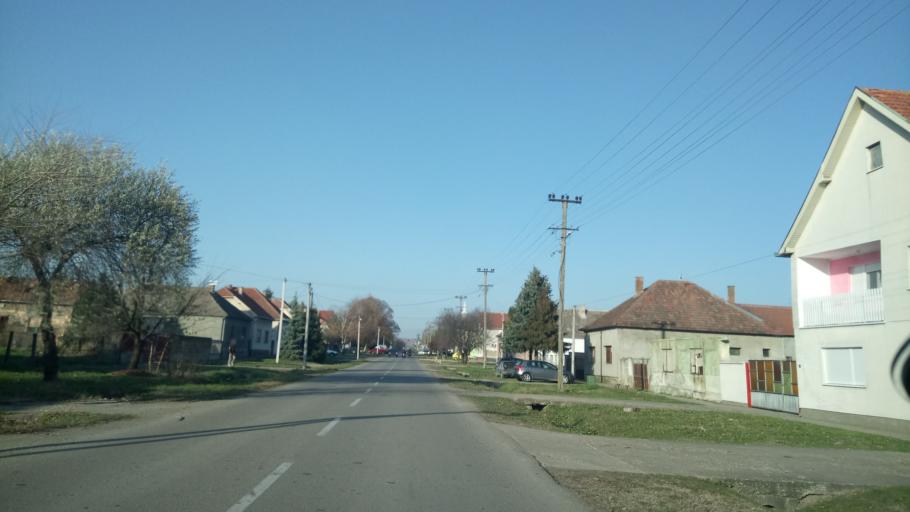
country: RS
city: Beska
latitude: 45.1267
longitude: 20.0674
